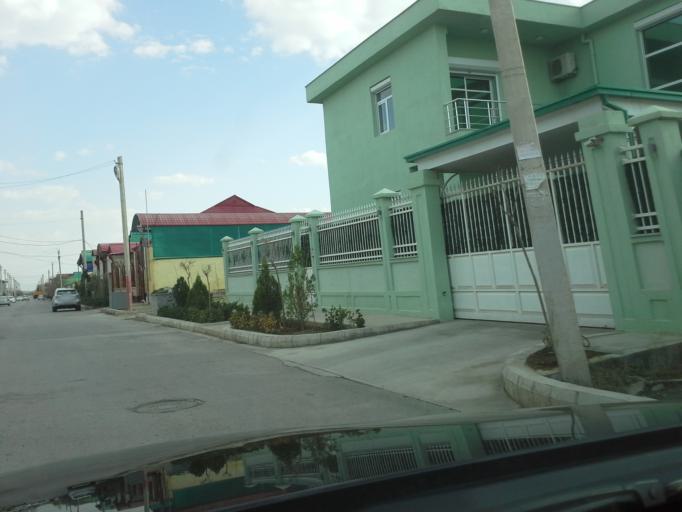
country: TM
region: Ahal
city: Ashgabat
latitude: 37.9956
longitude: 58.2947
